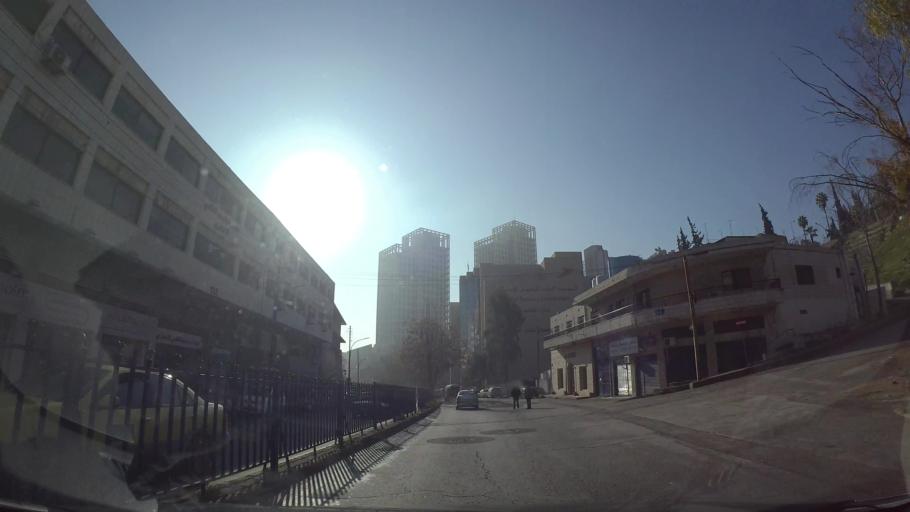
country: JO
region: Amman
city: Amman
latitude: 31.9585
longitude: 35.9078
